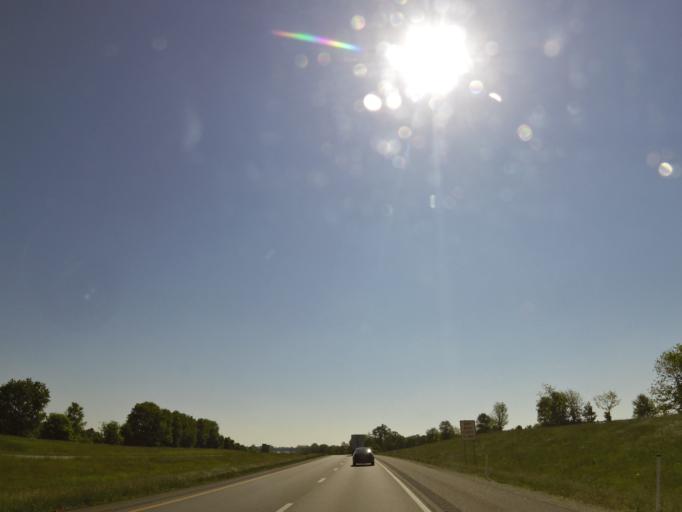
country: US
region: Kentucky
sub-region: Woodford County
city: Midway
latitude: 38.1589
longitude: -84.6583
